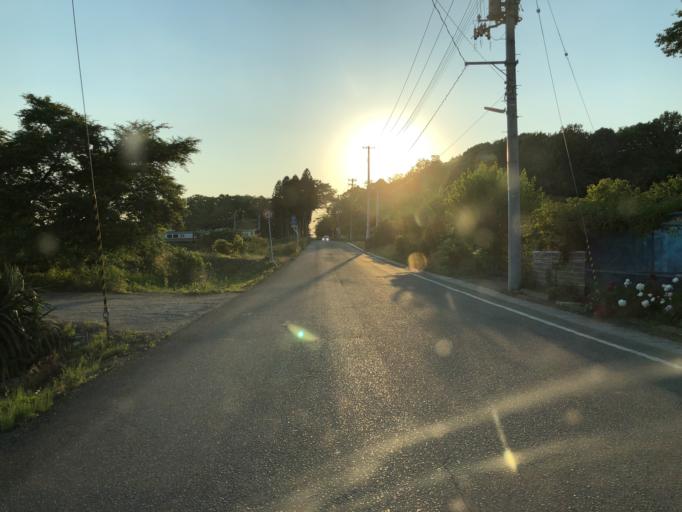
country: JP
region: Fukushima
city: Sukagawa
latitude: 37.1852
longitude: 140.3112
